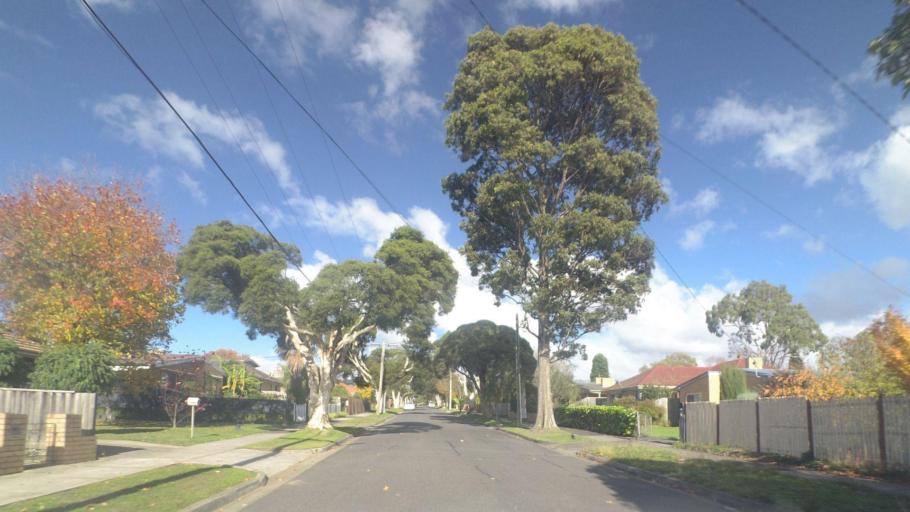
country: AU
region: Victoria
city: Forest Hill
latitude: -37.8400
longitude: 145.1824
